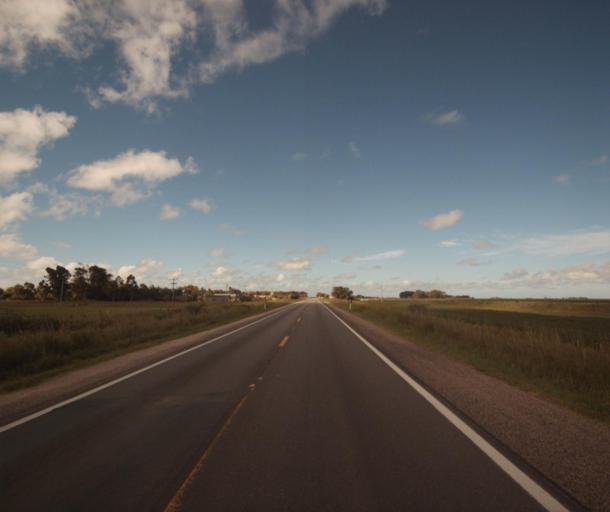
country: UY
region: Cerro Largo
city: Rio Branco
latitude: -32.9450
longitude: -52.7712
